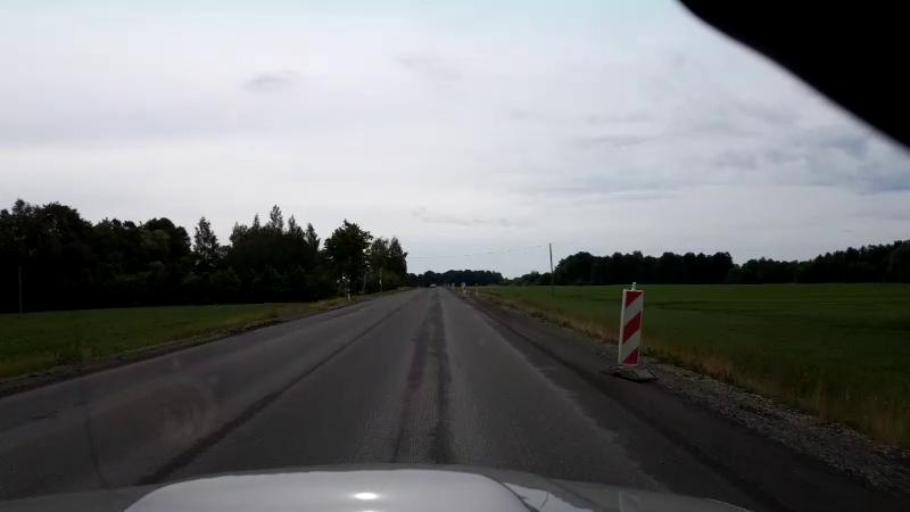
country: LV
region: Bauskas Rajons
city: Bauska
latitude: 56.2976
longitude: 24.3454
